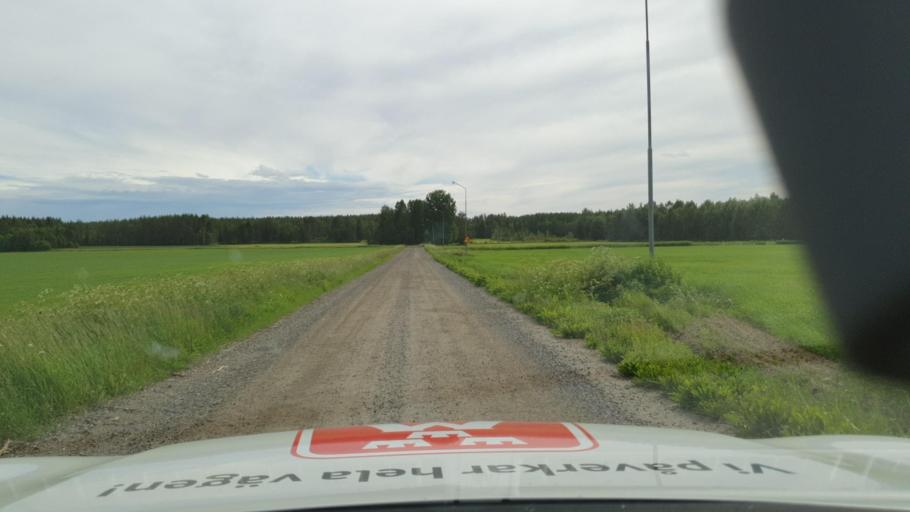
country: SE
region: Vaesterbotten
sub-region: Robertsfors Kommun
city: Robertsfors
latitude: 64.3799
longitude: 21.0348
